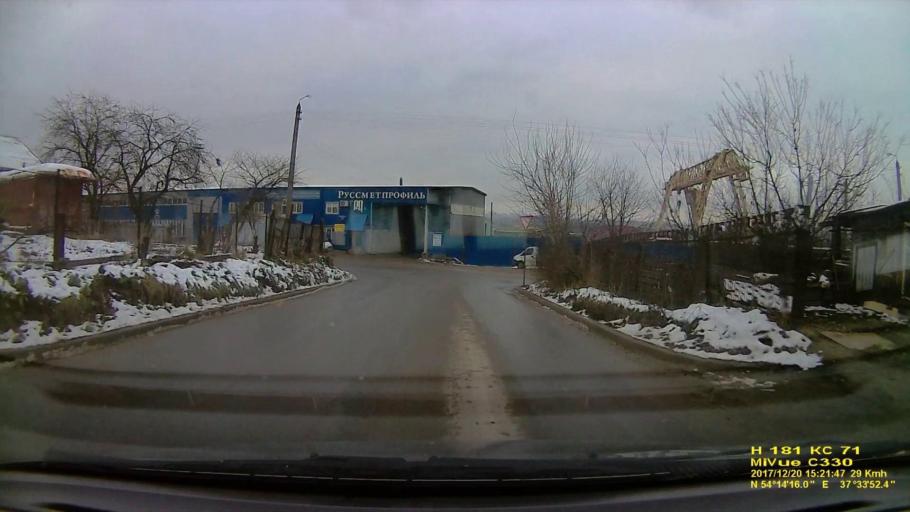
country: RU
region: Tula
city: Gorelki
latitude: 54.2377
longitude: 37.5646
